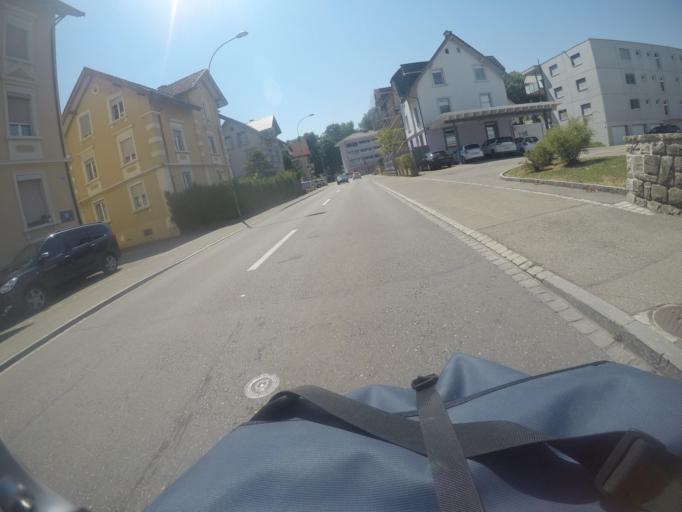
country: CH
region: Thurgau
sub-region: Arbon District
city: Arbon
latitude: 47.5112
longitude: 9.4254
